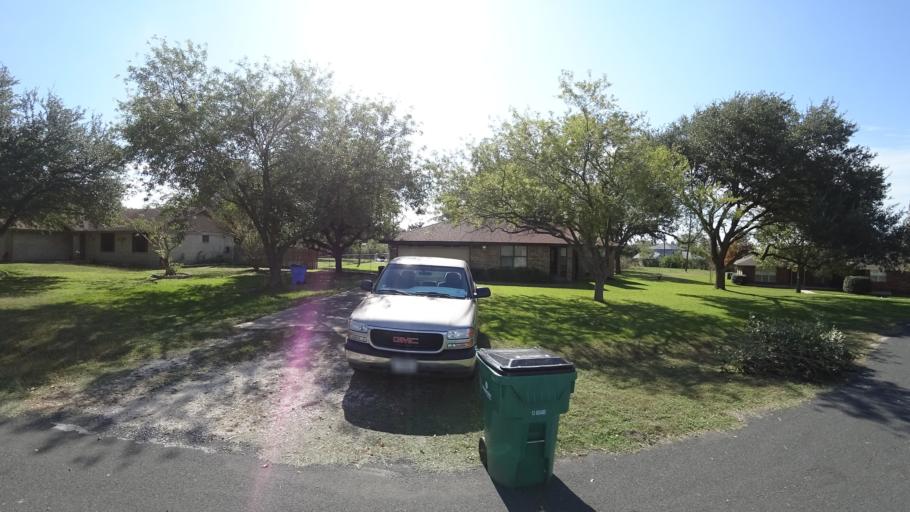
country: US
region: Texas
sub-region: Travis County
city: Pflugerville
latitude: 30.4166
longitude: -97.6298
